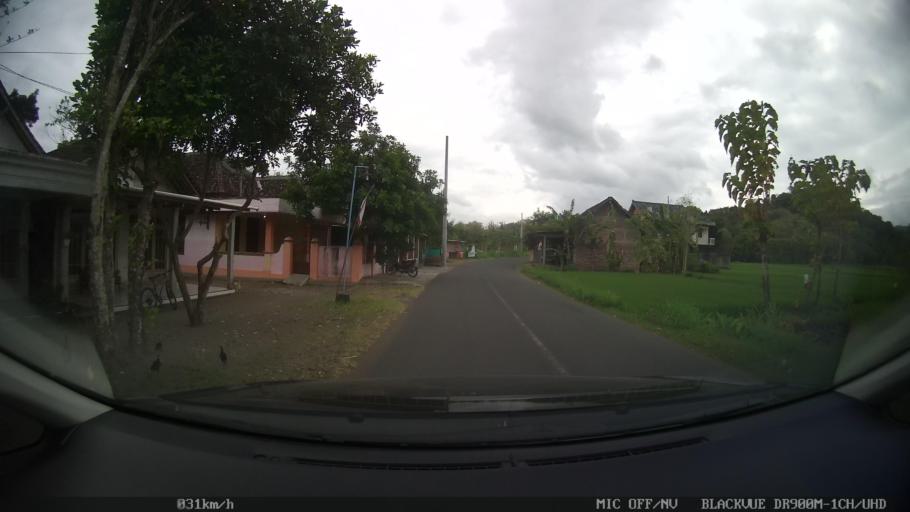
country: ID
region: Daerah Istimewa Yogyakarta
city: Sewon
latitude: -7.8692
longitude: 110.4188
